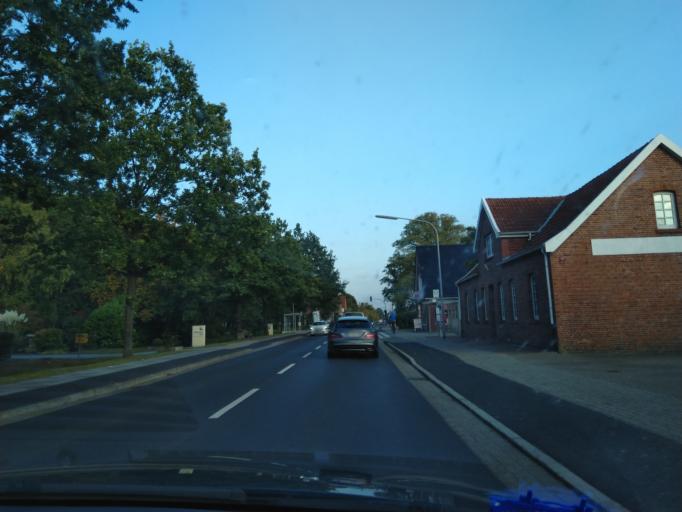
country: DE
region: Lower Saxony
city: Papenburg
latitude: 53.0755
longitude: 7.4094
